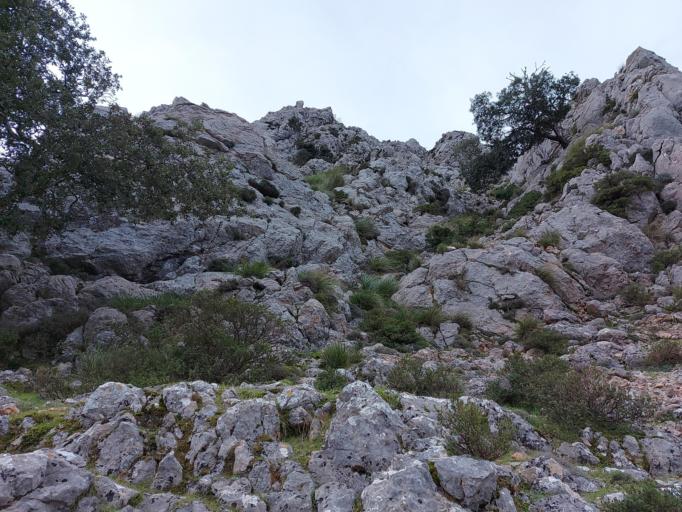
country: ES
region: Balearic Islands
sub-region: Illes Balears
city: Escorca
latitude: 39.8156
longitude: 2.8670
